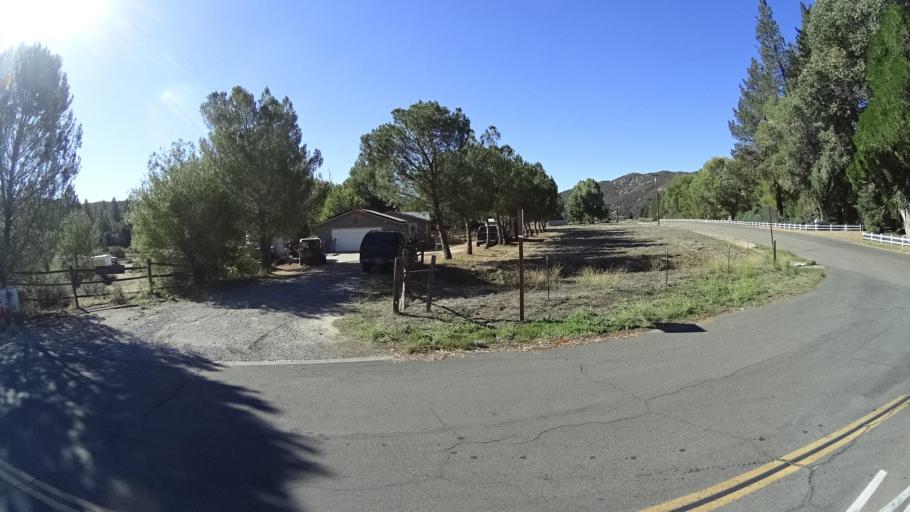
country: US
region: California
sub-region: San Diego County
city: Pine Valley
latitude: 32.8434
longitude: -116.5280
